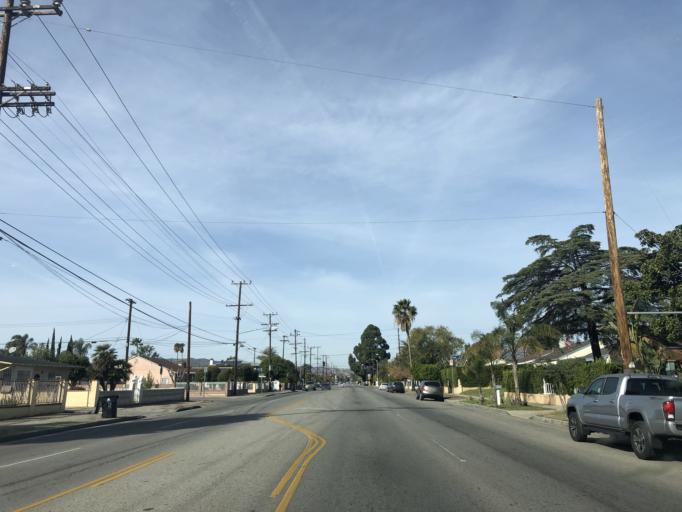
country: US
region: California
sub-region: Los Angeles County
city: San Fernando
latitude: 34.2545
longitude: -118.4276
